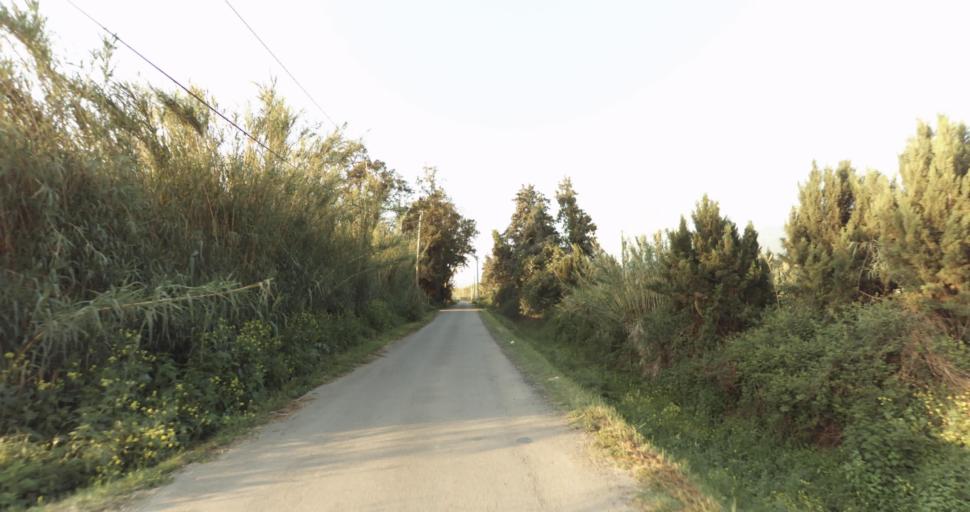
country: FR
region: Corsica
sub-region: Departement de la Haute-Corse
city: Biguglia
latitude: 42.6168
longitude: 9.4457
